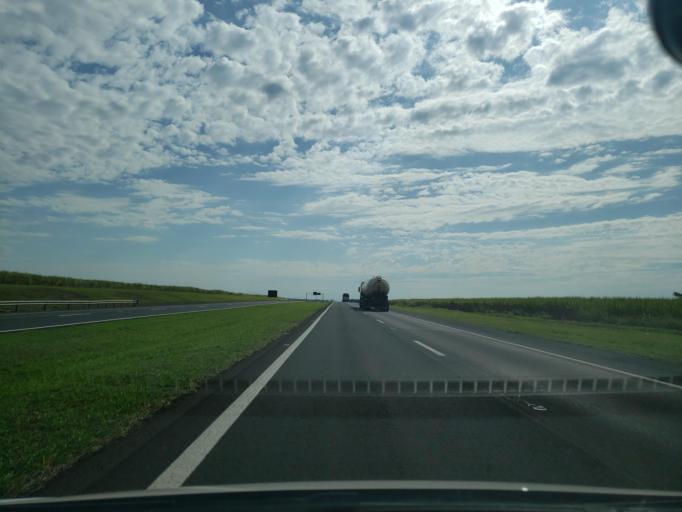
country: BR
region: Sao Paulo
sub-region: Promissao
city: Promissao
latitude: -21.6179
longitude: -49.8587
